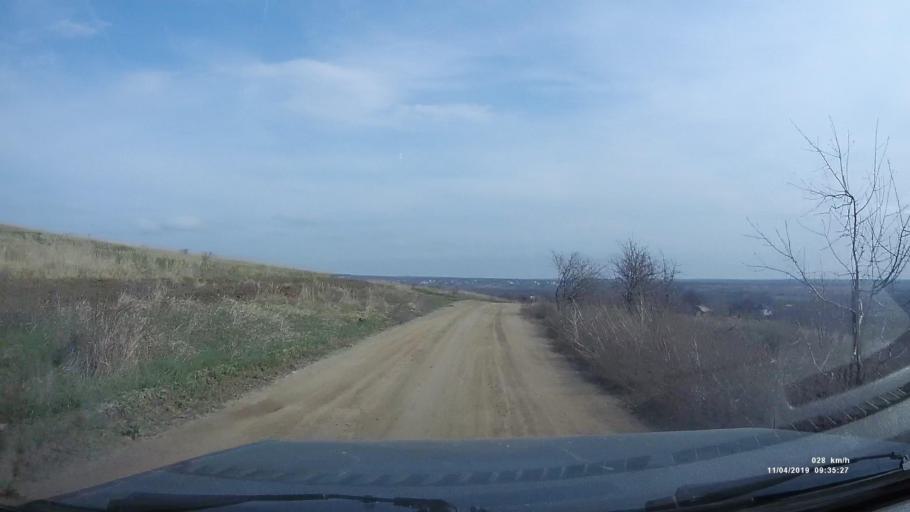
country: RU
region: Rostov
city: Staraya Stanitsa
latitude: 48.2725
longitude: 40.3718
